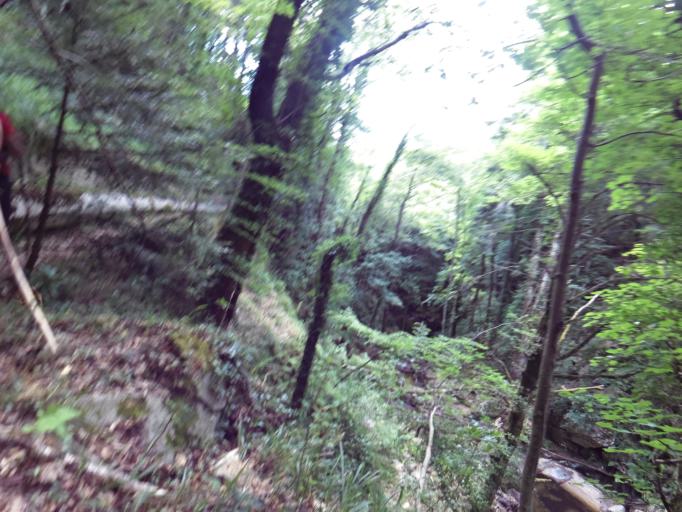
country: IT
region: Calabria
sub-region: Provincia di Vibo-Valentia
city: Nardodipace
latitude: 38.5077
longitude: 16.3826
